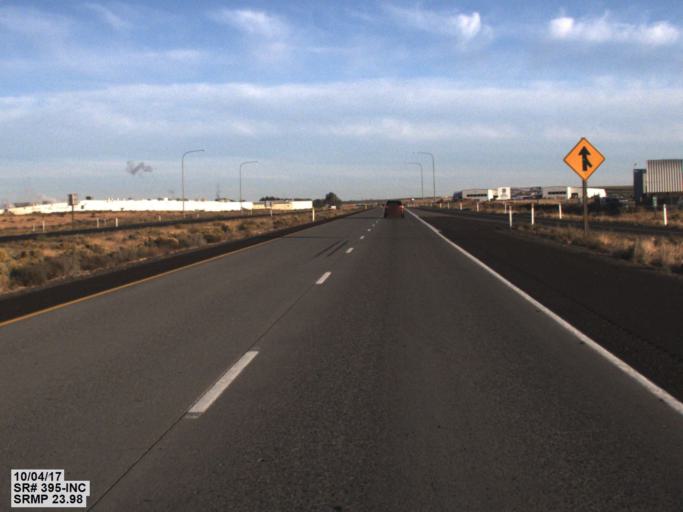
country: US
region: Washington
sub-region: Franklin County
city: Pasco
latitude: 46.2691
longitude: -119.0880
